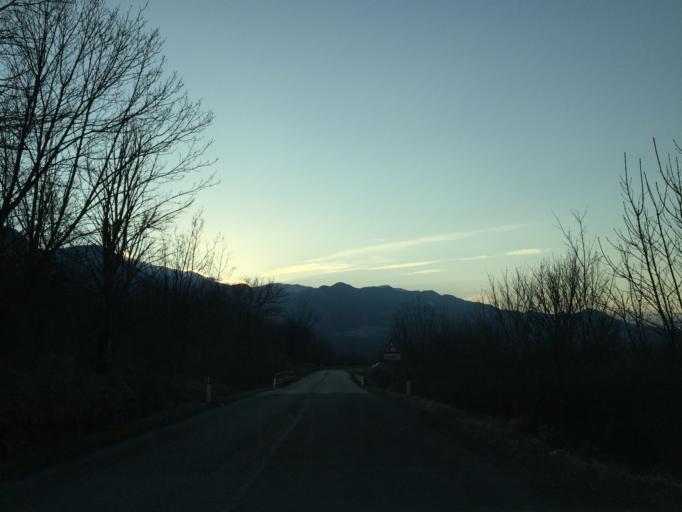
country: IT
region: Molise
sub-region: Provincia di Campobasso
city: Guardiaregia
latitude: 41.4490
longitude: 14.5521
